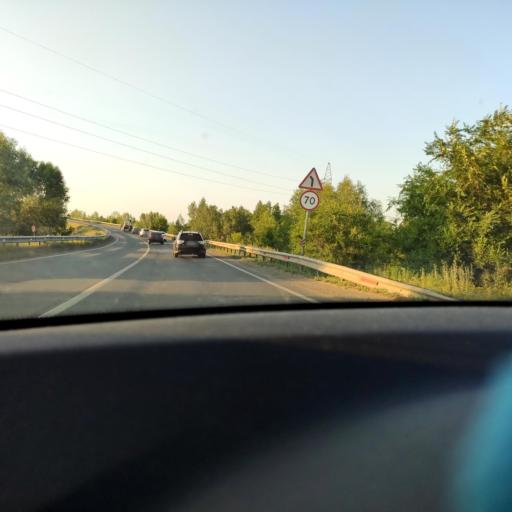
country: RU
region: Samara
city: Kinel'
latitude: 53.2486
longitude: 50.5907
